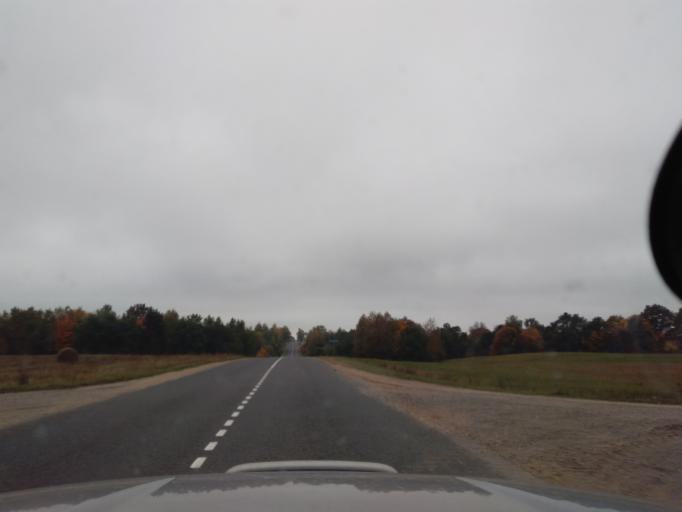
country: BY
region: Minsk
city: Kapyl'
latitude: 53.1501
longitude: 27.2063
